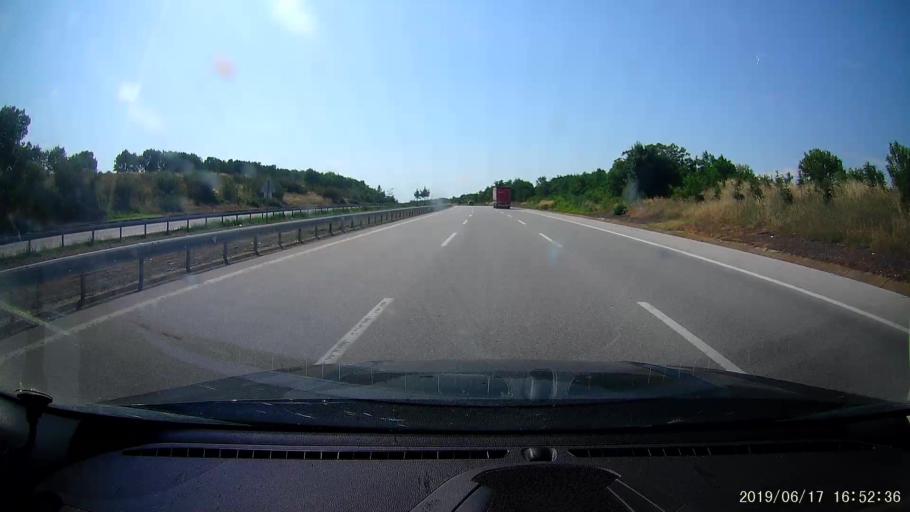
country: TR
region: Kirklareli
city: Inece
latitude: 41.5567
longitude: 27.0480
